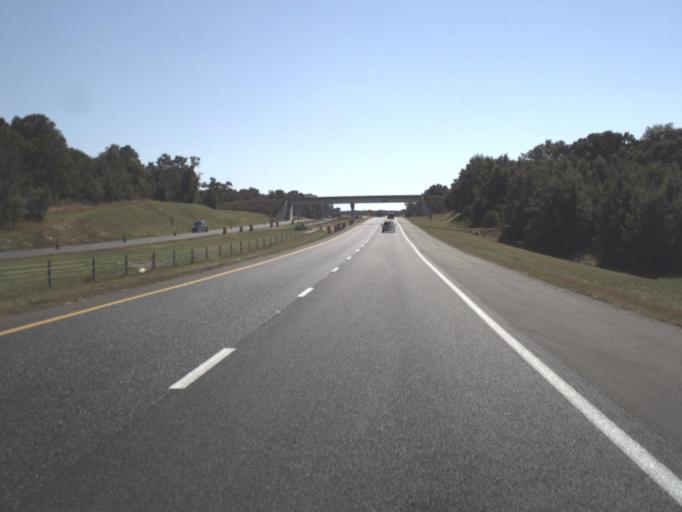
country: US
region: Florida
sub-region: Hernando County
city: Brookridge
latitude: 28.5990
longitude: -82.4896
